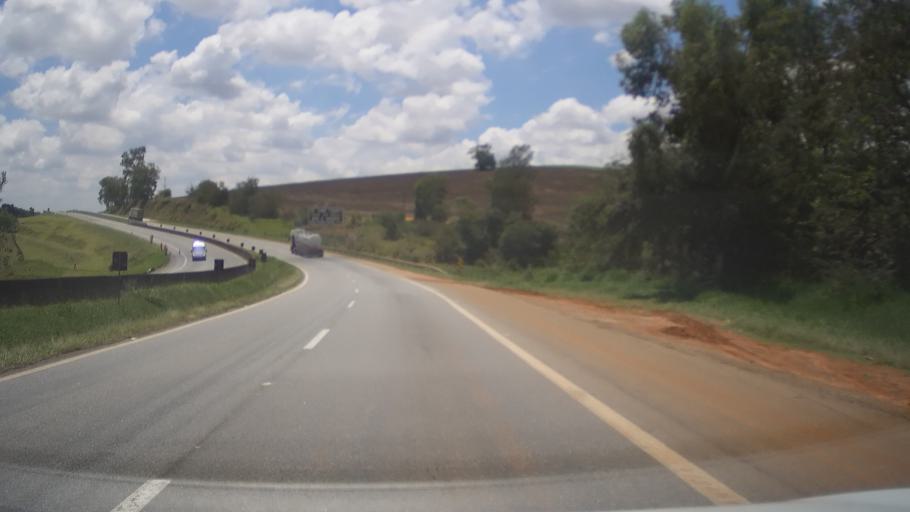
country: BR
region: Minas Gerais
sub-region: Campanha
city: Campanha
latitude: -21.8051
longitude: -45.4755
